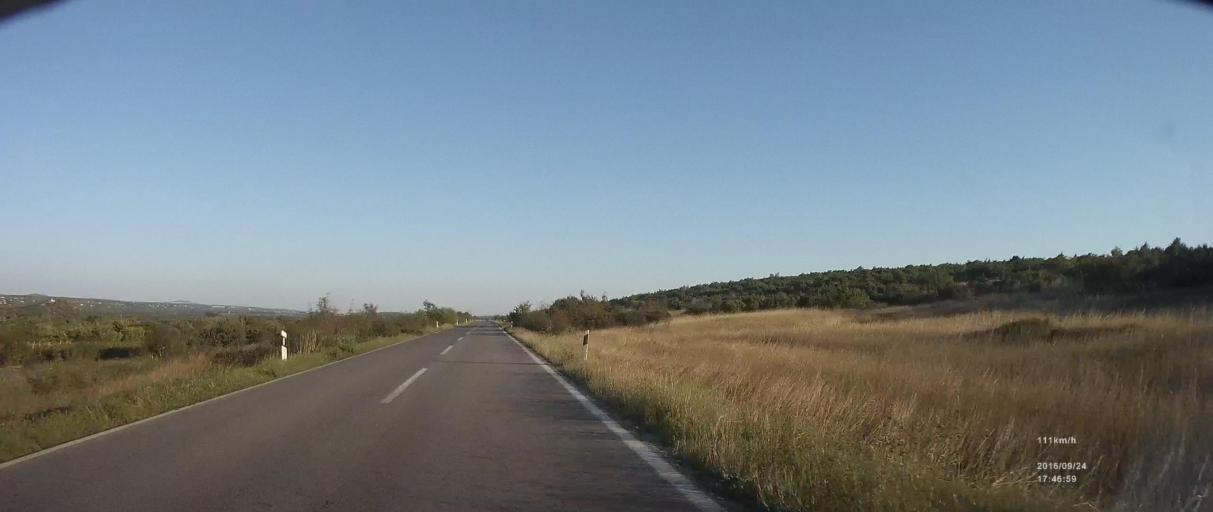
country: HR
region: Zadarska
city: Polaca
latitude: 44.0807
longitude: 15.5160
